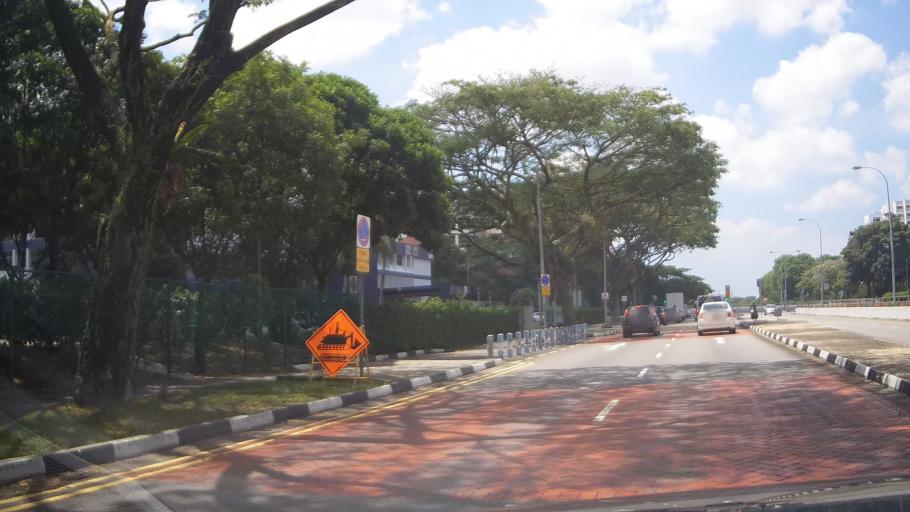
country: MY
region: Johor
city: Johor Bahru
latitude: 1.3514
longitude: 103.7283
